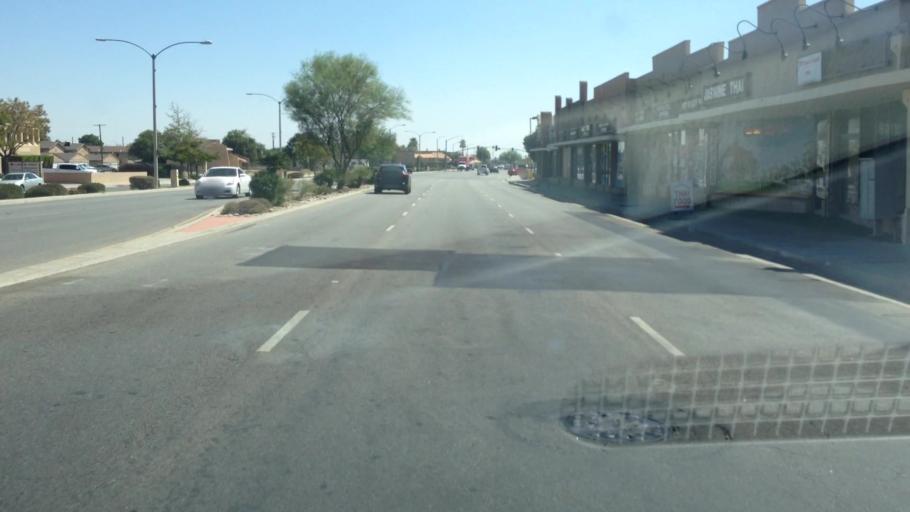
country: US
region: California
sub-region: Los Angeles County
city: Palmdale
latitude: 34.5798
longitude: -118.1241
